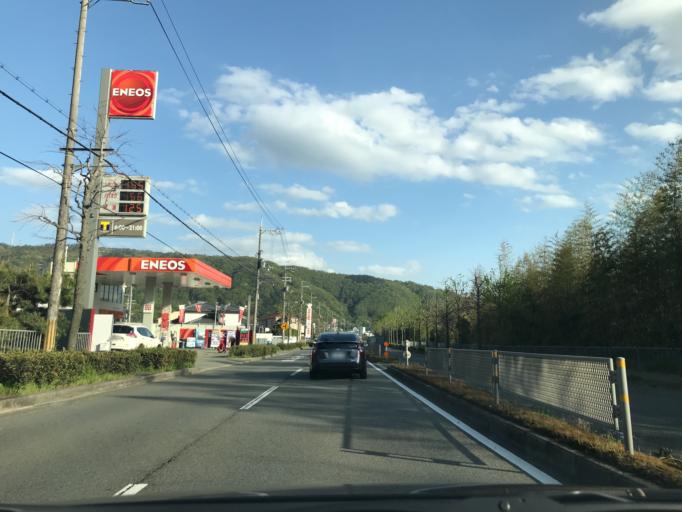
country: JP
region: Osaka
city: Ikeda
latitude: 34.8492
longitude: 135.4196
